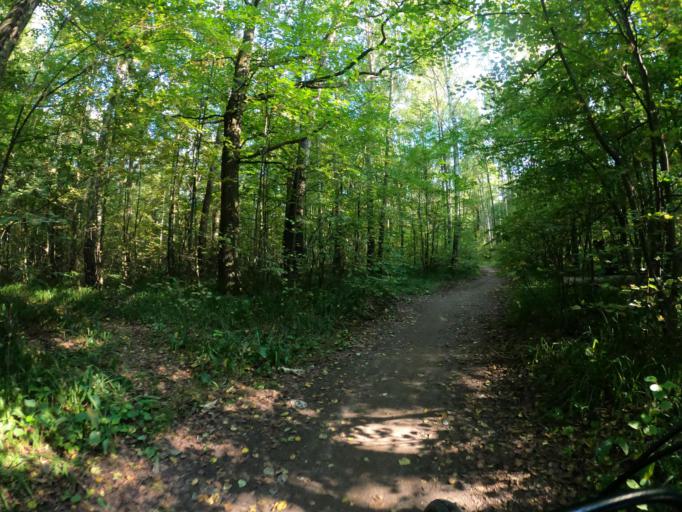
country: RU
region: Moskovskaya
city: Stupino
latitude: 54.8801
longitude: 38.0882
